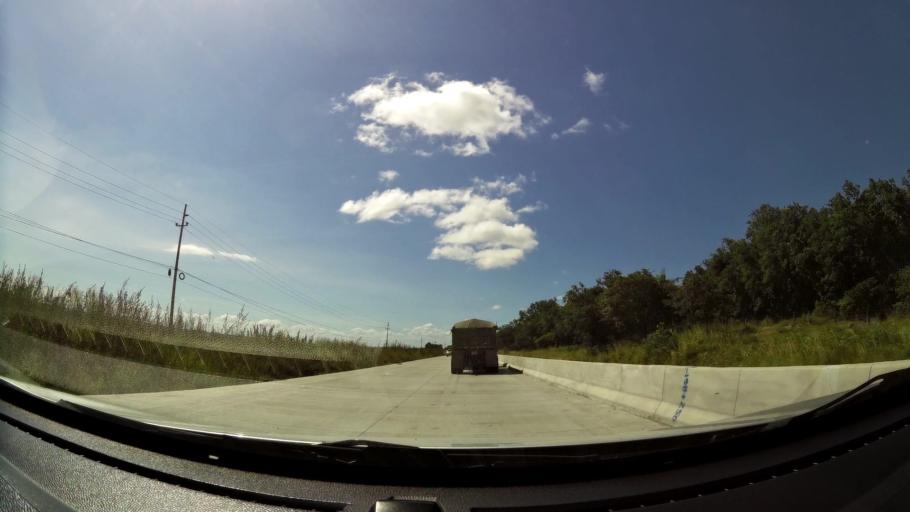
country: CR
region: Guanacaste
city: Bagaces
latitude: 10.5391
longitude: -85.3259
